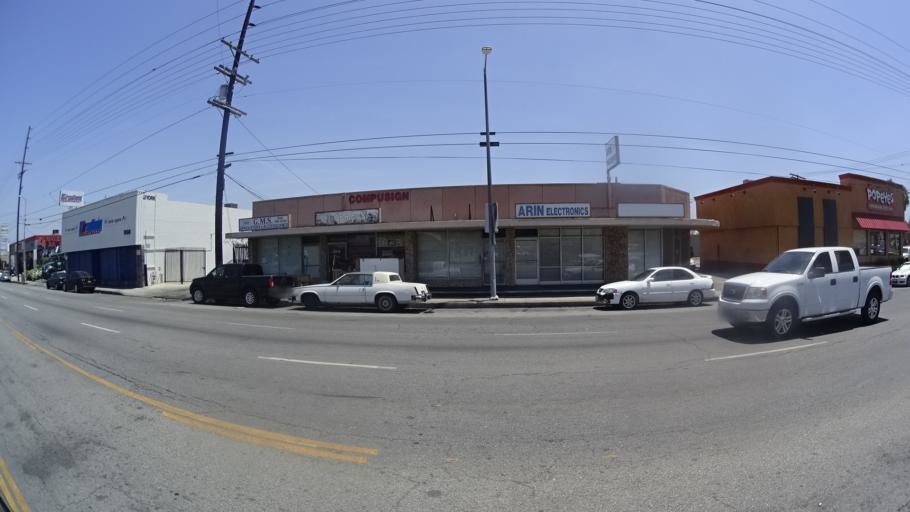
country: US
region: California
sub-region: Los Angeles County
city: Van Nuys
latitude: 34.2090
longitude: -118.4663
